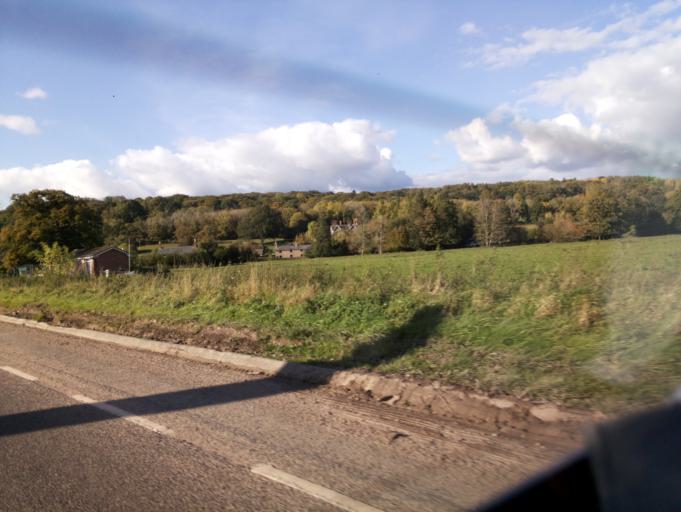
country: GB
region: England
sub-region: Herefordshire
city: Clifford
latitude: 52.1192
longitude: -3.0669
